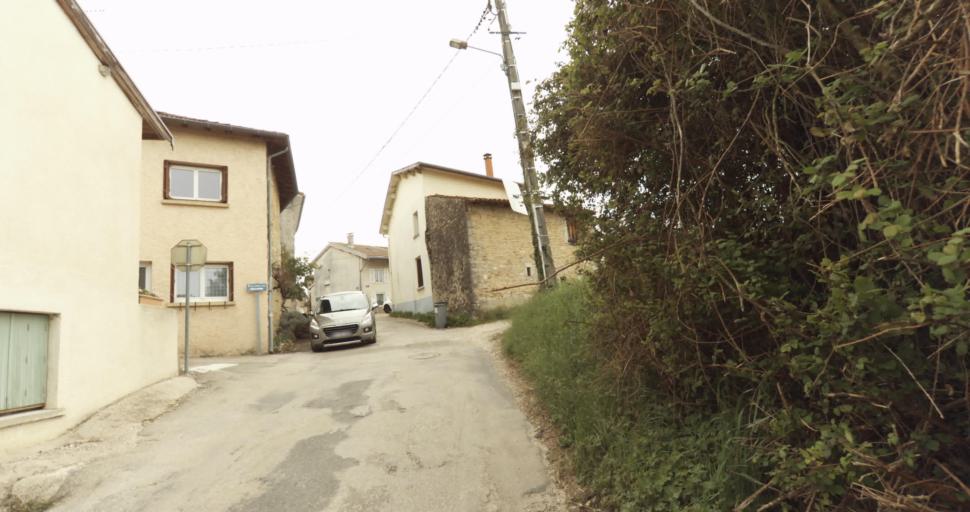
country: FR
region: Rhone-Alpes
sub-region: Departement de l'Ain
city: Amberieu-en-Bugey
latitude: 45.9661
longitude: 5.3625
